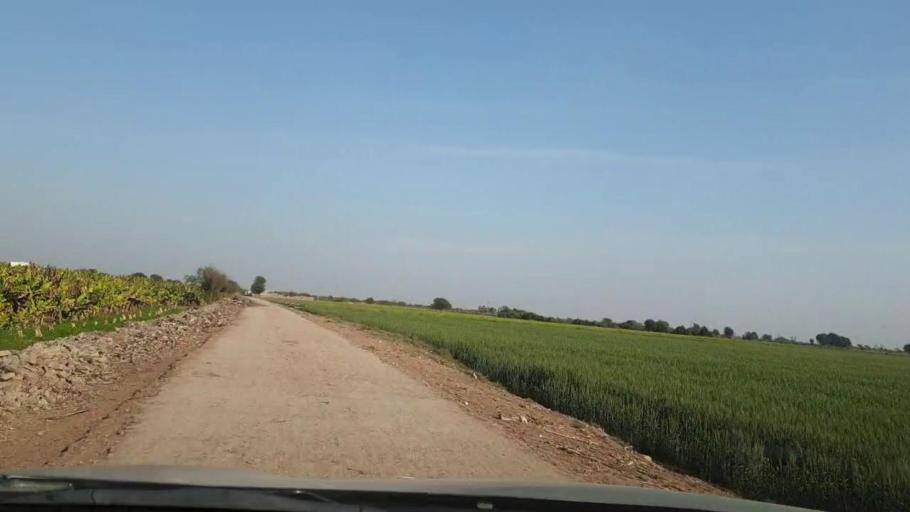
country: PK
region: Sindh
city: Berani
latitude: 25.7271
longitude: 68.7788
